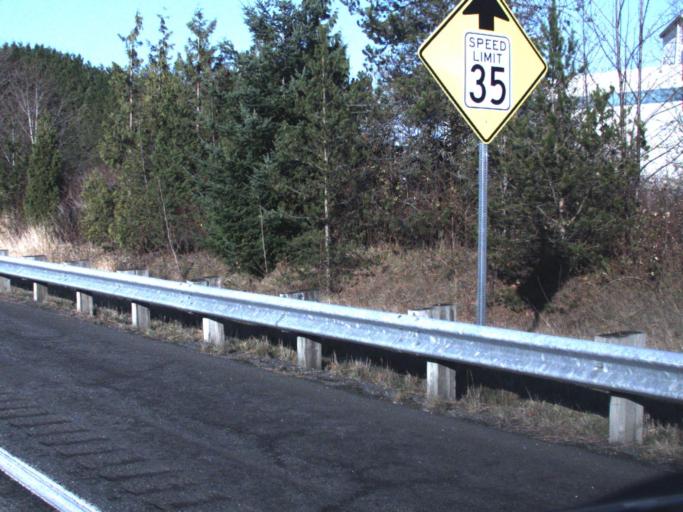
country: US
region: Washington
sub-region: Whatcom County
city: Blaine
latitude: 48.9879
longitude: -122.7372
